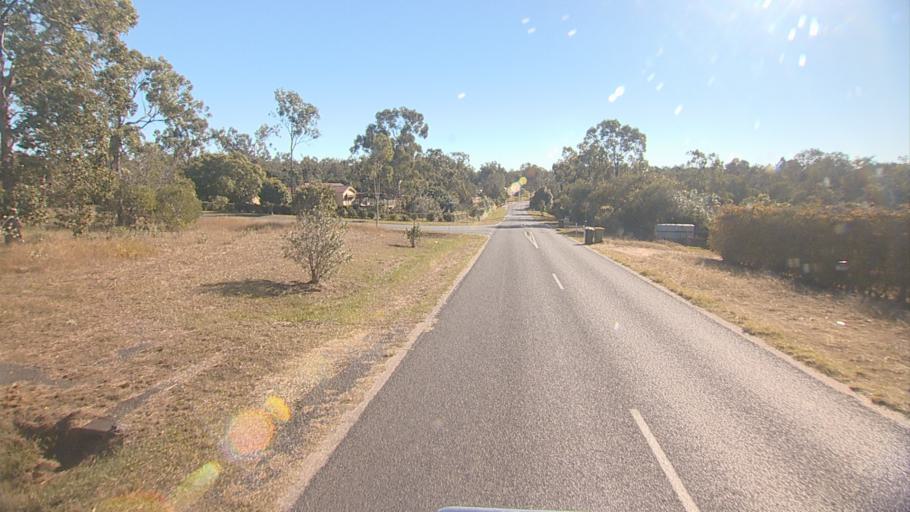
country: AU
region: Queensland
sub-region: Logan
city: North Maclean
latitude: -27.7450
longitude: 152.9677
